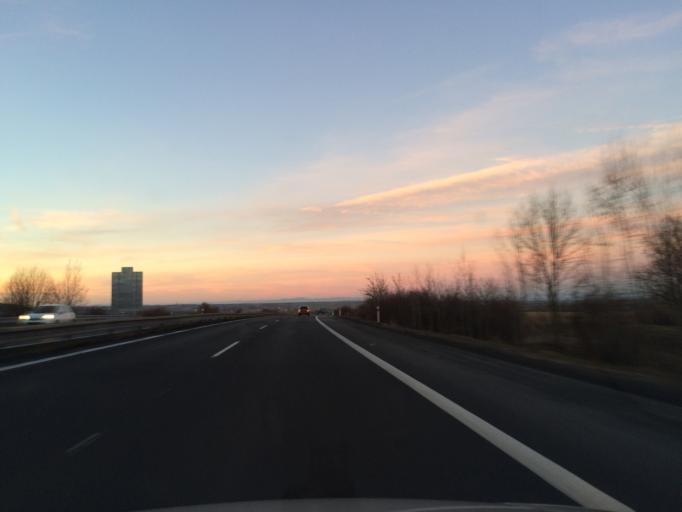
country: CZ
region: Central Bohemia
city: Bustehrad
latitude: 50.1533
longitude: 14.2152
